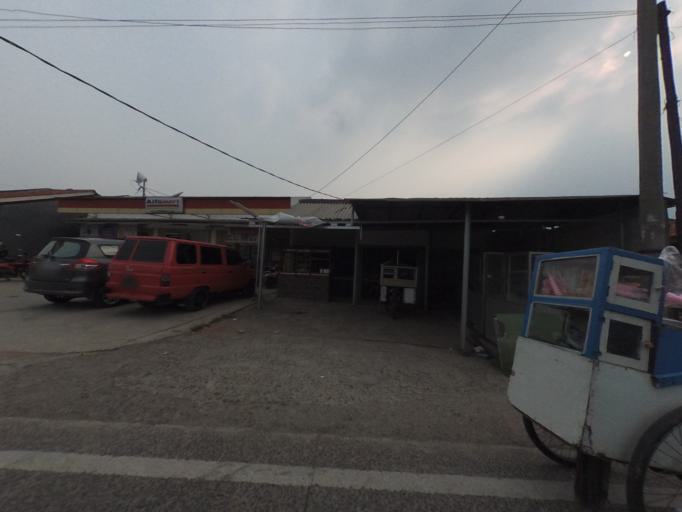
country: ID
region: West Java
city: Sidoger Lebak
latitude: -6.5657
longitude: 106.5930
